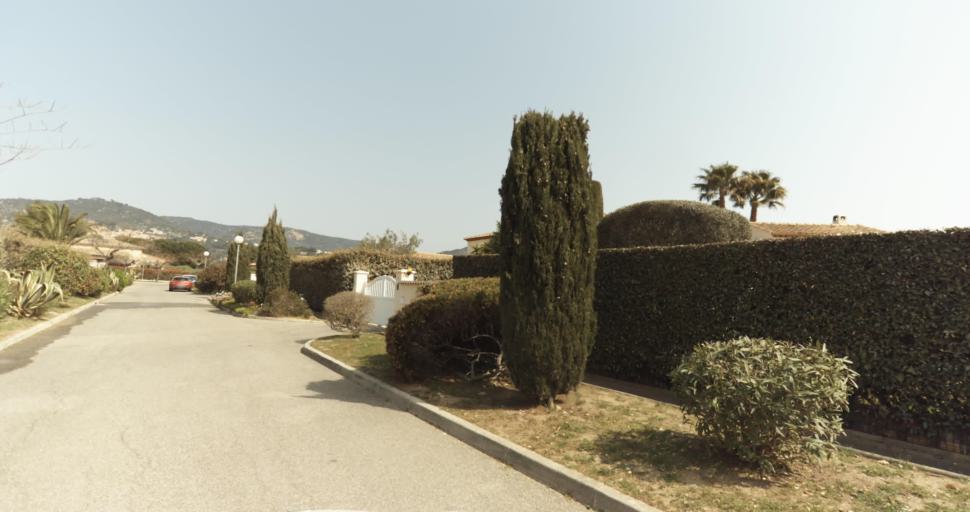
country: FR
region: Provence-Alpes-Cote d'Azur
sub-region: Departement du Var
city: Bormes-les-Mimosas
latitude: 43.1347
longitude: 6.3423
